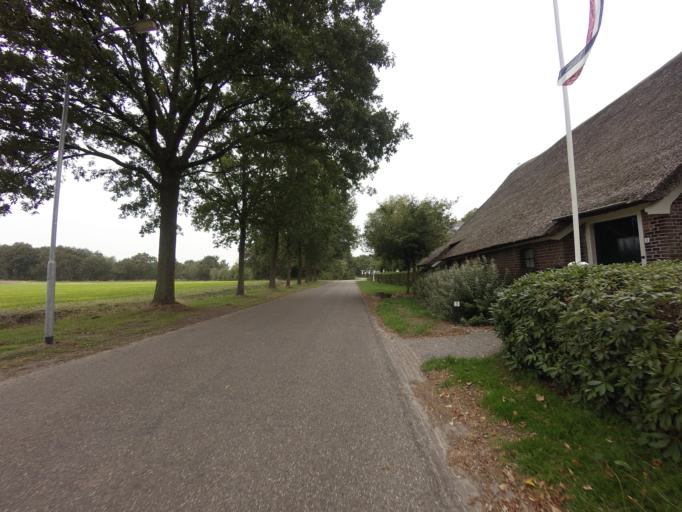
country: NL
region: Drenthe
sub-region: Gemeente Assen
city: Assen
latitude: 52.9991
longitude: 6.6342
